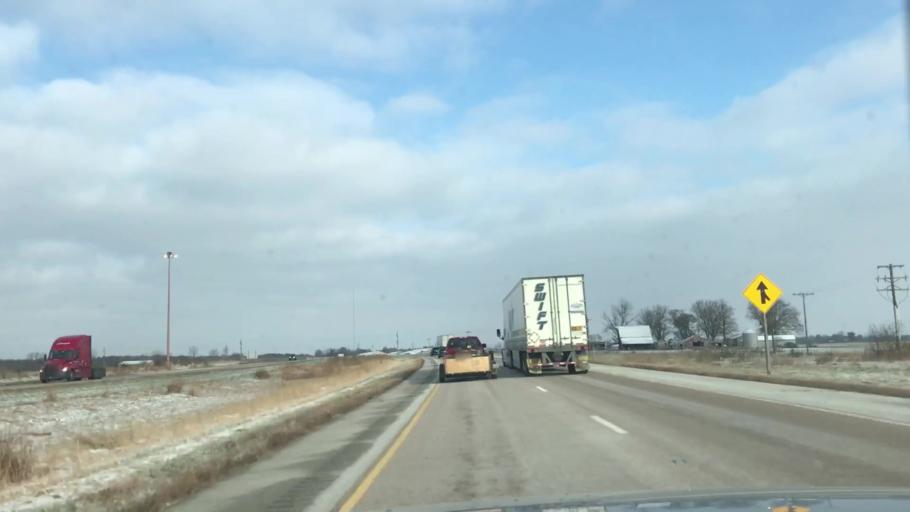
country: US
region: Illinois
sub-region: Macoupin County
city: Staunton
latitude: 39.0237
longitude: -89.7497
